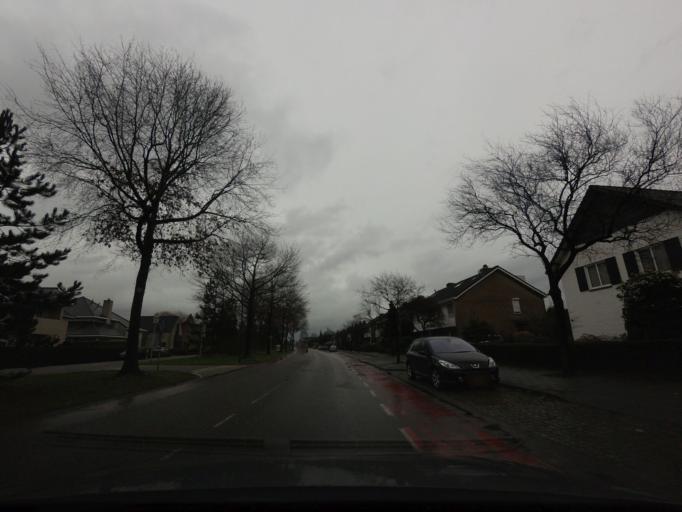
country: NL
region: North Brabant
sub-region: Gemeente Breda
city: Breda
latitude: 51.6043
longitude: 4.7108
